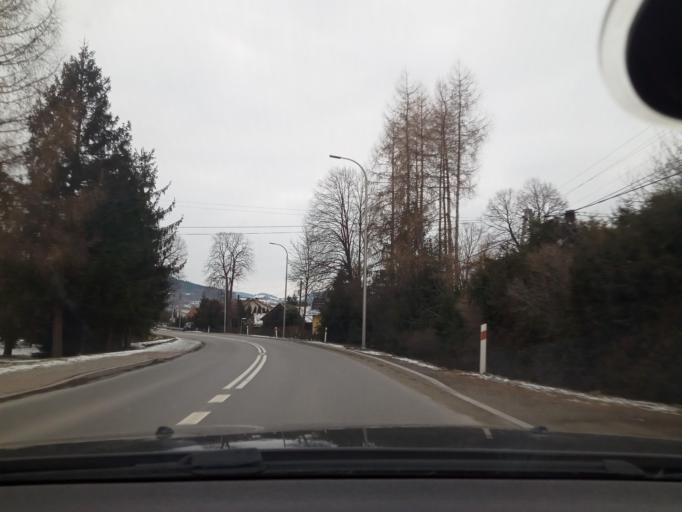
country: PL
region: Lesser Poland Voivodeship
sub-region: Powiat limanowski
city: Kamienica
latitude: 49.5760
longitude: 20.3419
